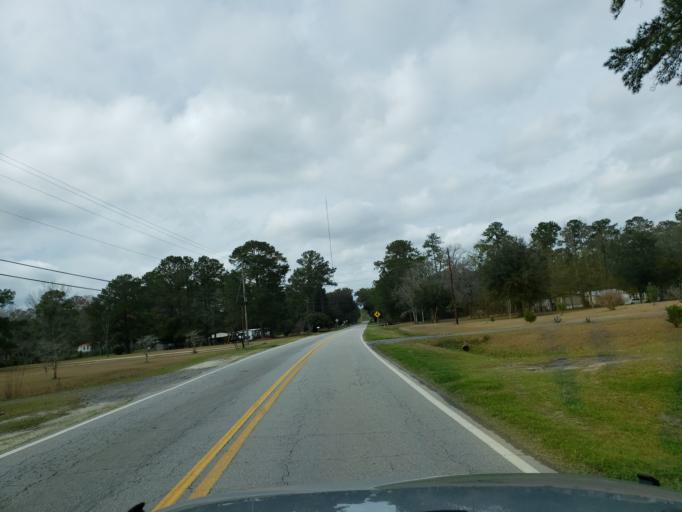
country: US
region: Georgia
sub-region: Chatham County
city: Pooler
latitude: 32.0474
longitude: -81.2842
